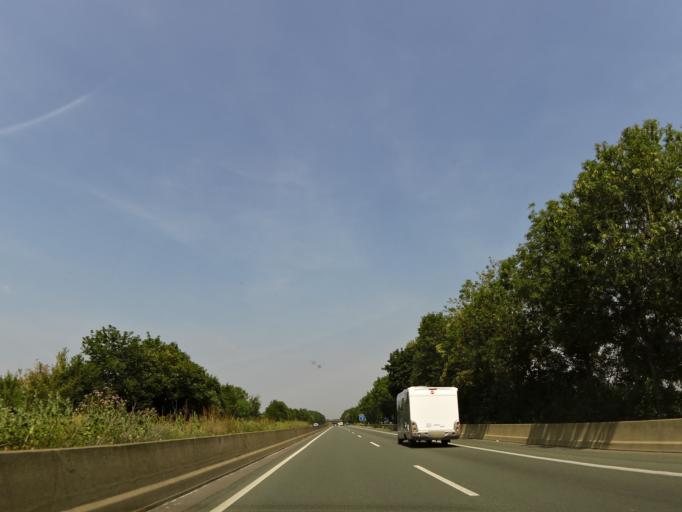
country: DE
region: North Rhine-Westphalia
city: Tuernich
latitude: 50.8315
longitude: 6.7678
